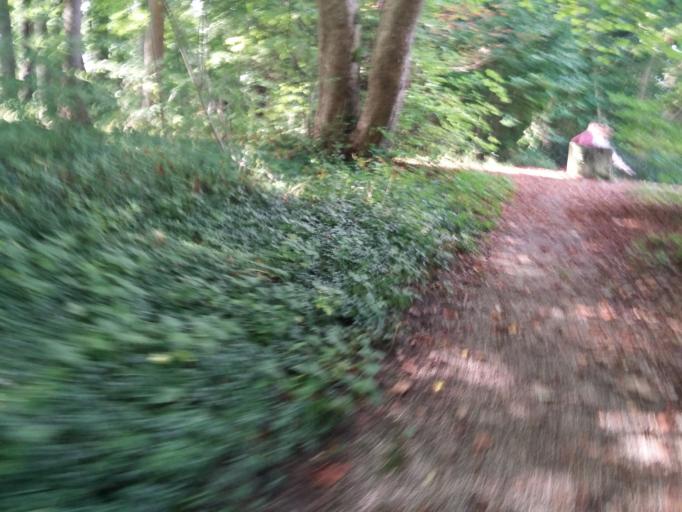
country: DE
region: Bavaria
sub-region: Upper Bavaria
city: Landsberg am Lech
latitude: 48.0438
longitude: 10.8761
